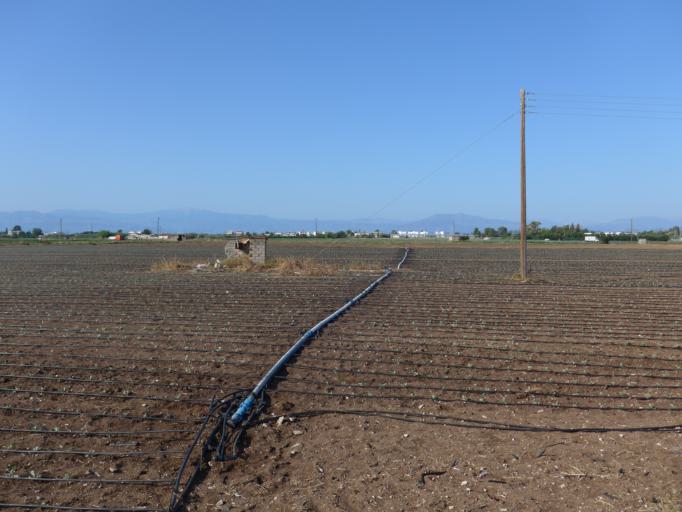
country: GR
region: Peloponnese
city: Asklipieio
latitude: 37.4956
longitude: 23.0020
